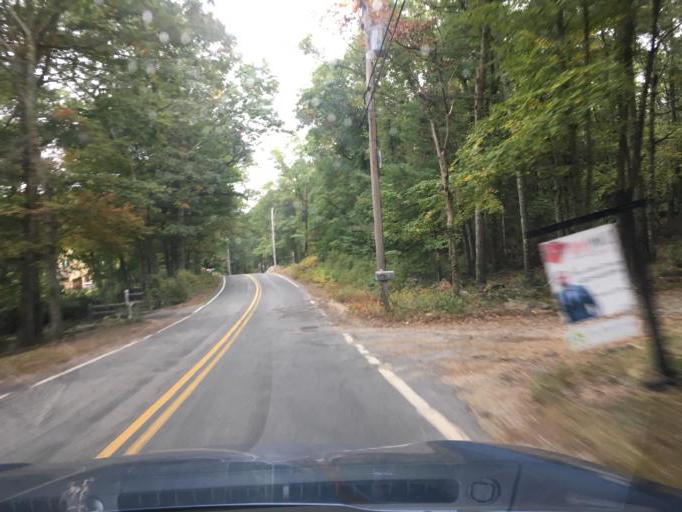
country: US
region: Rhode Island
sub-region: Washington County
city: Exeter
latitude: 41.6111
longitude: -71.5651
